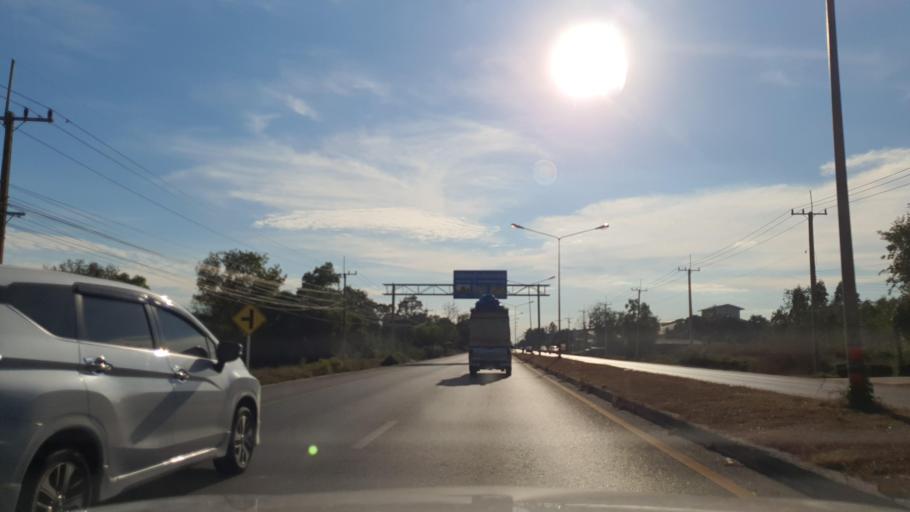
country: TH
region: Kalasin
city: Yang Talat
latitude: 16.3602
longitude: 103.3378
